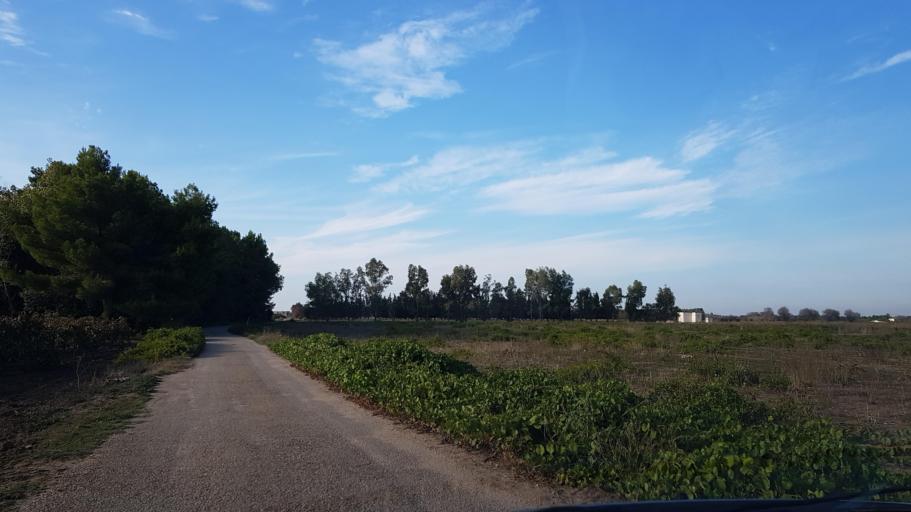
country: IT
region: Apulia
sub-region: Provincia di Brindisi
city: San Pancrazio Salentino
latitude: 40.4909
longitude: 17.8553
